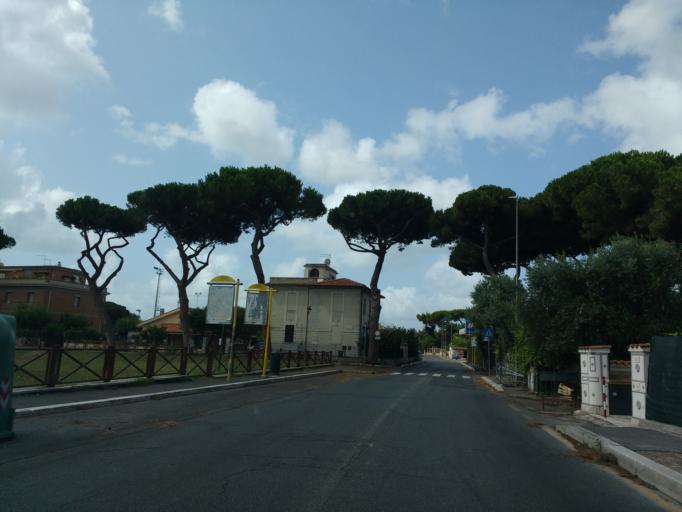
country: IT
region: Latium
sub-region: Citta metropolitana di Roma Capitale
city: Acilia-Castel Fusano-Ostia Antica
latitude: 41.7585
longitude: 12.3002
